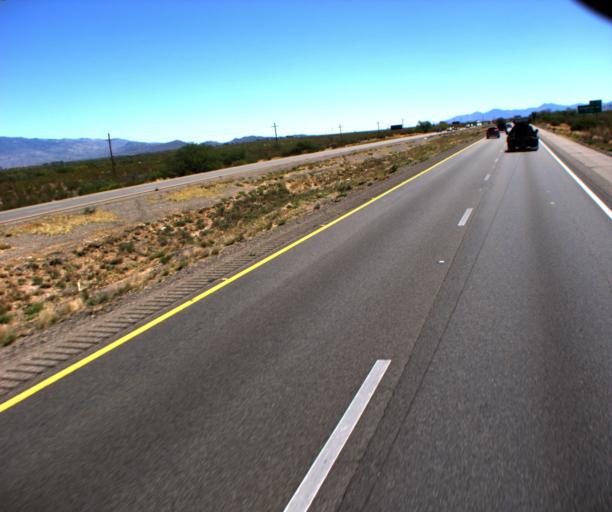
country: US
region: Arizona
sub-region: Pima County
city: Vail
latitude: 32.0737
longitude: -110.7932
